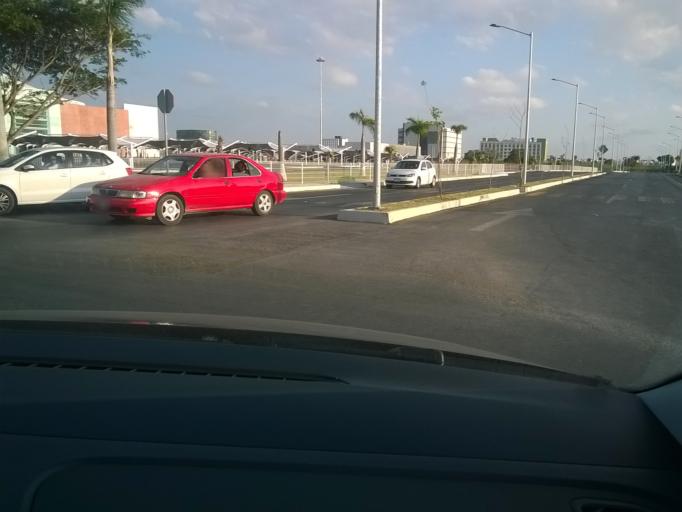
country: MX
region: Yucatan
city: Merida
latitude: 21.0398
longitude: -89.6348
